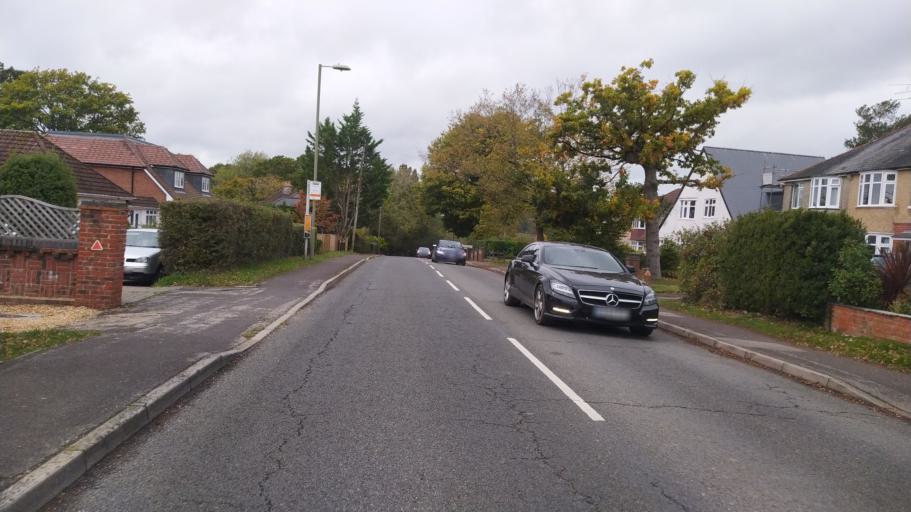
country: GB
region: England
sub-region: Hampshire
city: Cowplain
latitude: 50.9030
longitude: -1.0169
